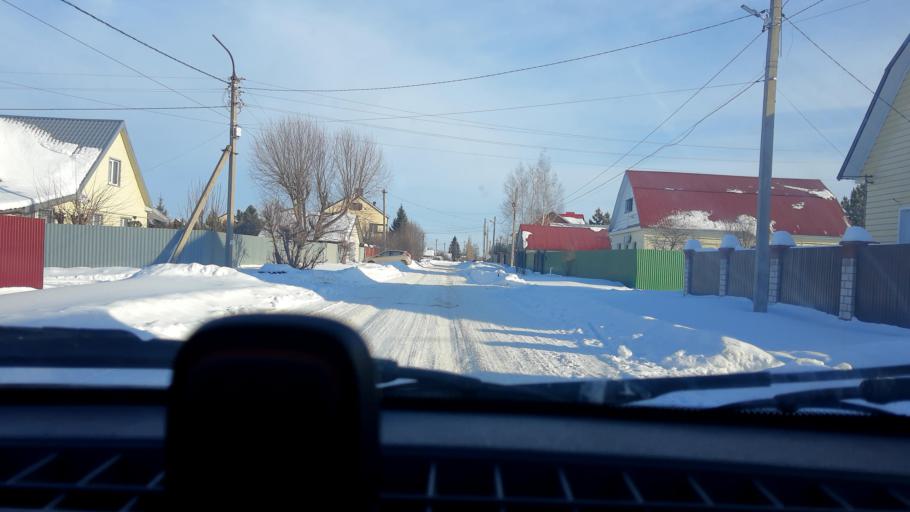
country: RU
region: Bashkortostan
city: Avdon
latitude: 54.4960
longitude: 55.8754
